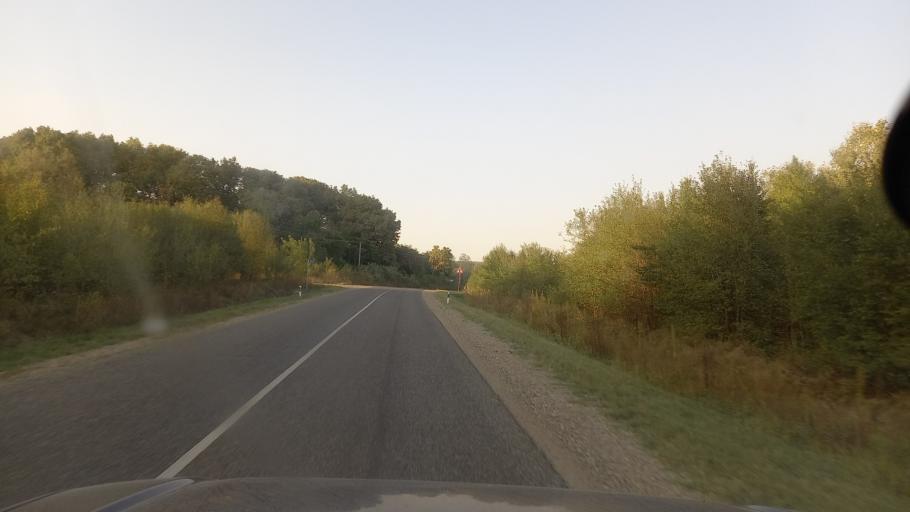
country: RU
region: Krasnodarskiy
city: Smolenskaya
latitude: 44.7515
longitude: 38.7626
